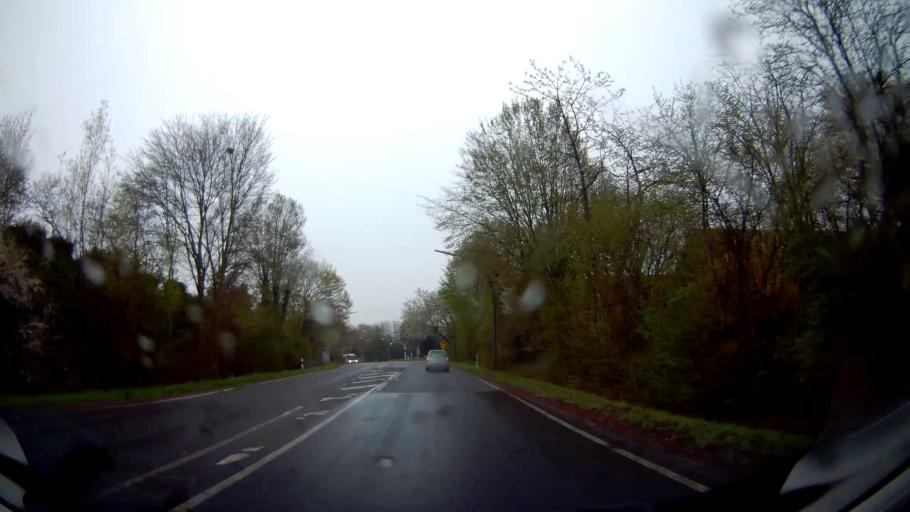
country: DE
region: North Rhine-Westphalia
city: Castrop-Rauxel
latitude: 51.5328
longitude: 7.3454
